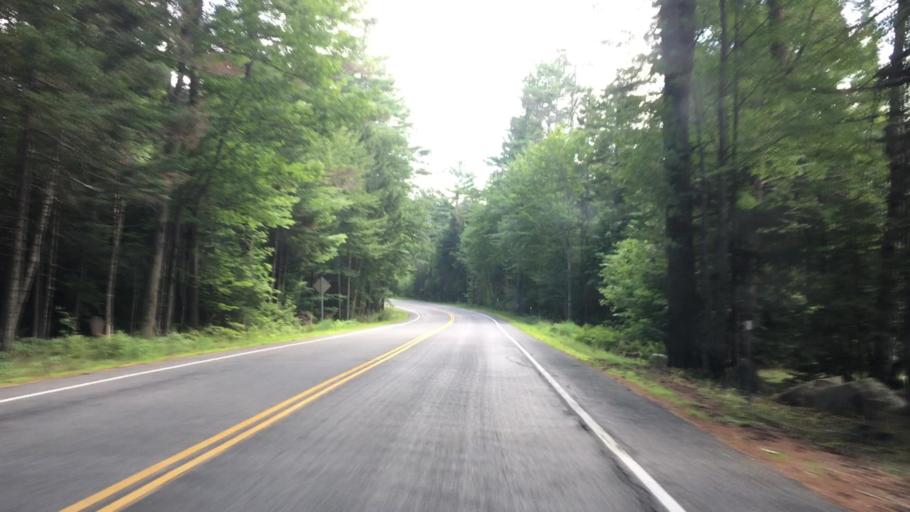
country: US
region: New Hampshire
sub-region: Grafton County
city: Woodstock
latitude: 44.0756
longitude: -71.7952
